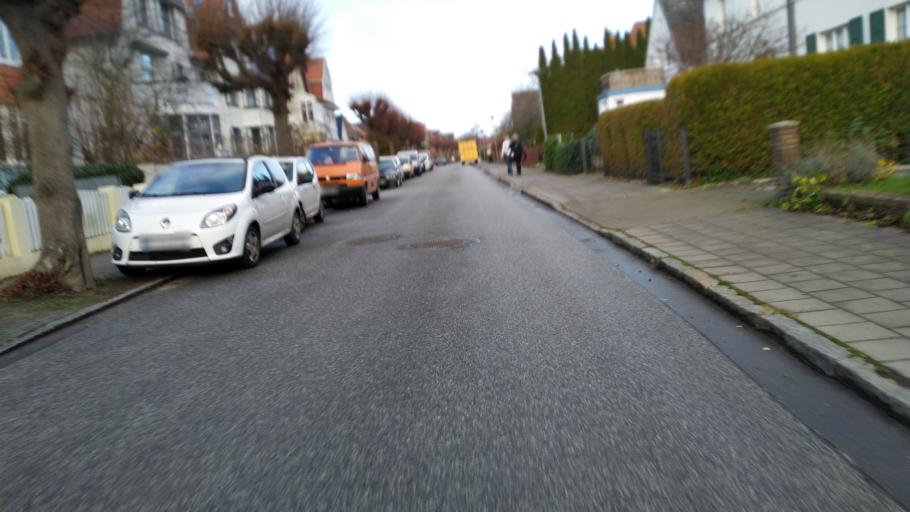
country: DE
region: Schleswig-Holstein
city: Travemuende
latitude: 53.9609
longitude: 10.8706
